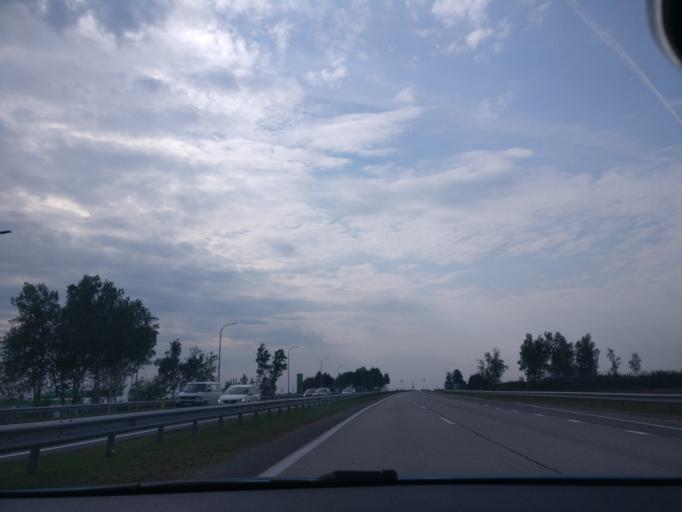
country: BY
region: Minsk
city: Lahoysk
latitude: 54.1680
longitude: 27.8184
